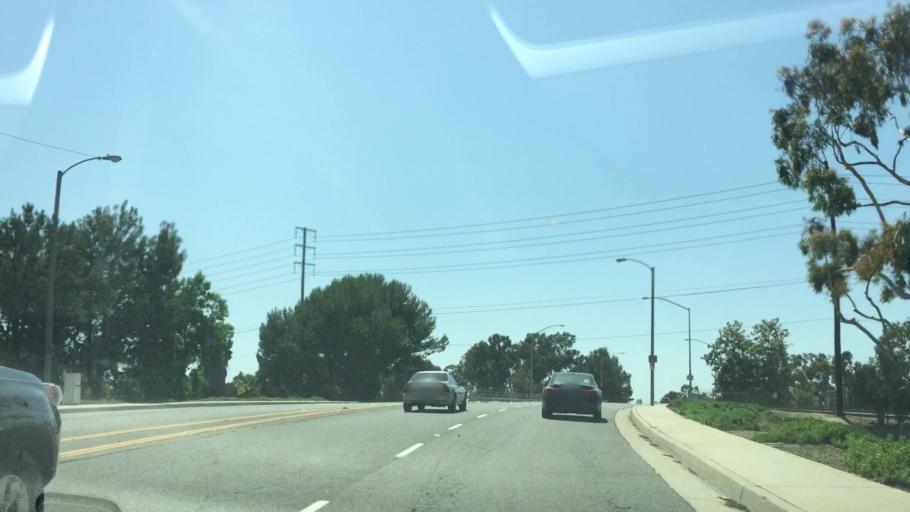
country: US
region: California
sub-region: Orange County
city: Fountain Valley
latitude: 33.7087
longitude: -117.9241
